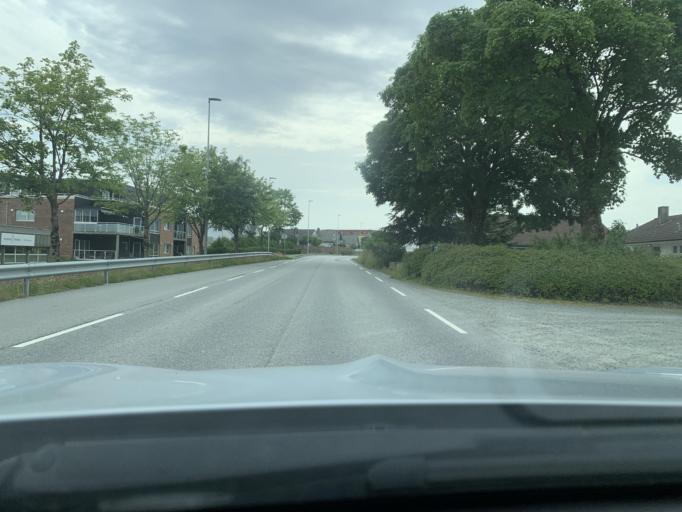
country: NO
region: Rogaland
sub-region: Sandnes
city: Sandnes
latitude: 58.7818
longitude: 5.7174
